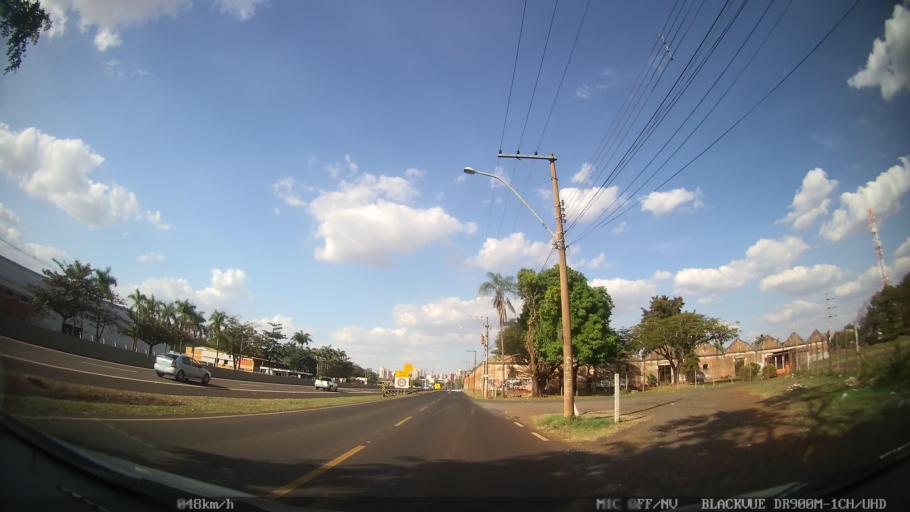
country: BR
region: Sao Paulo
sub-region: Ribeirao Preto
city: Ribeirao Preto
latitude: -21.1784
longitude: -47.8284
